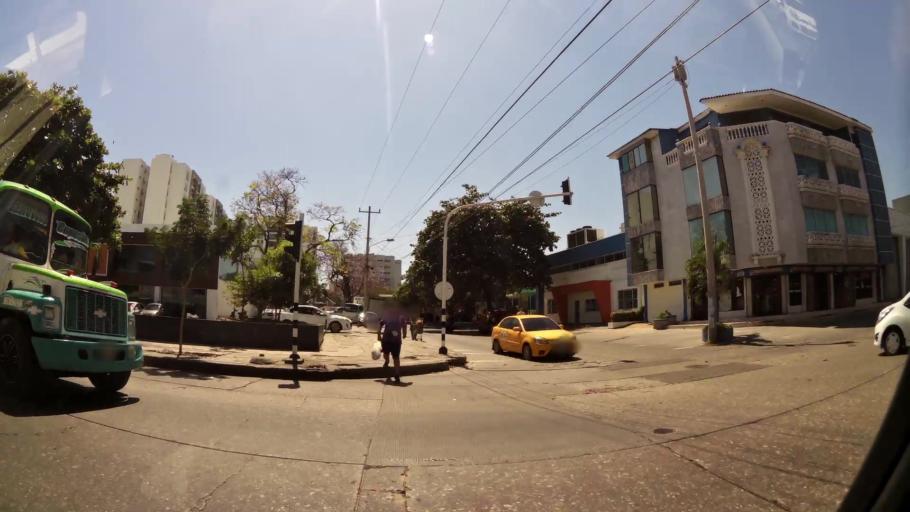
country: CO
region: Atlantico
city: Barranquilla
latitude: 10.9864
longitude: -74.7975
